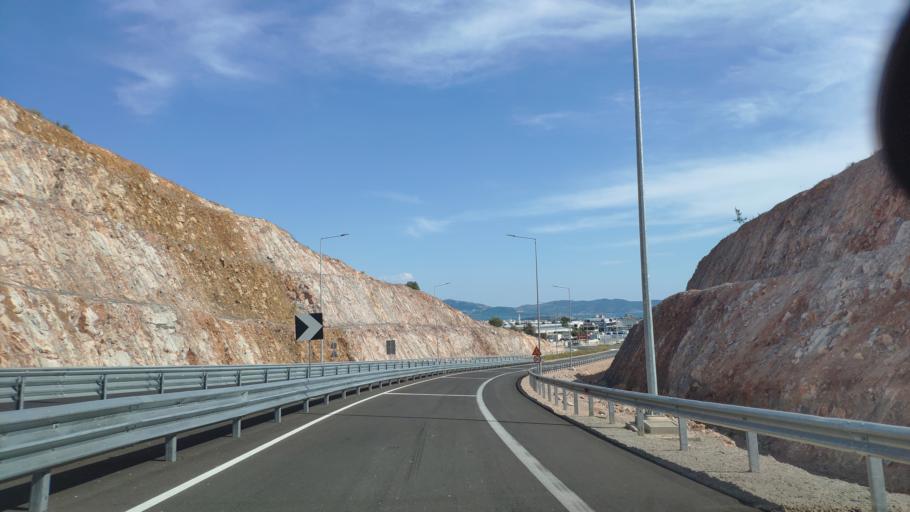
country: GR
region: Attica
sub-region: Nomarchia Dytikis Attikis
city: Mandra
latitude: 38.0795
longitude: 23.5062
